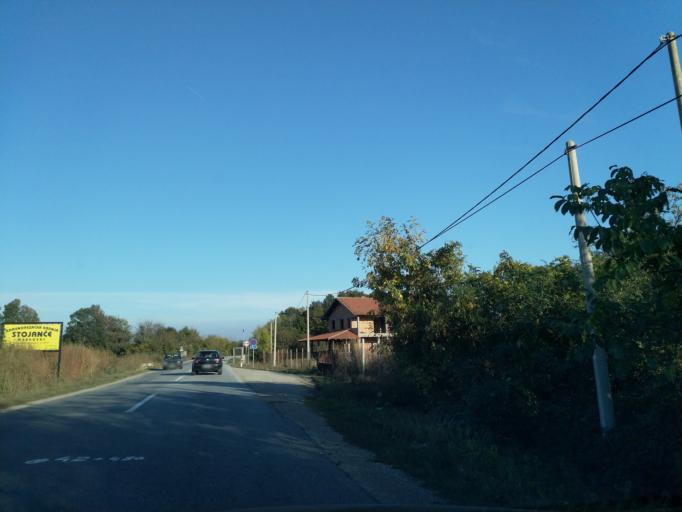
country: RS
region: Central Serbia
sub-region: Sumadijski Okrug
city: Lapovo
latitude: 44.2377
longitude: 21.1297
